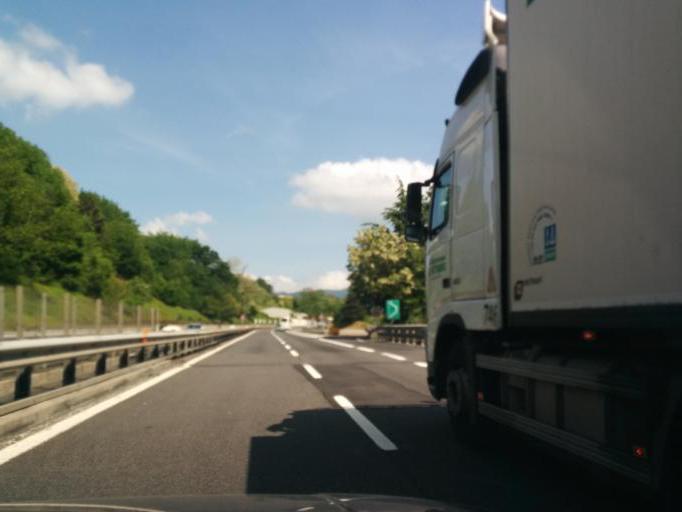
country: IT
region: Tuscany
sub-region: Province of Florence
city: Barberino di Mugello
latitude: 44.0225
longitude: 11.2228
